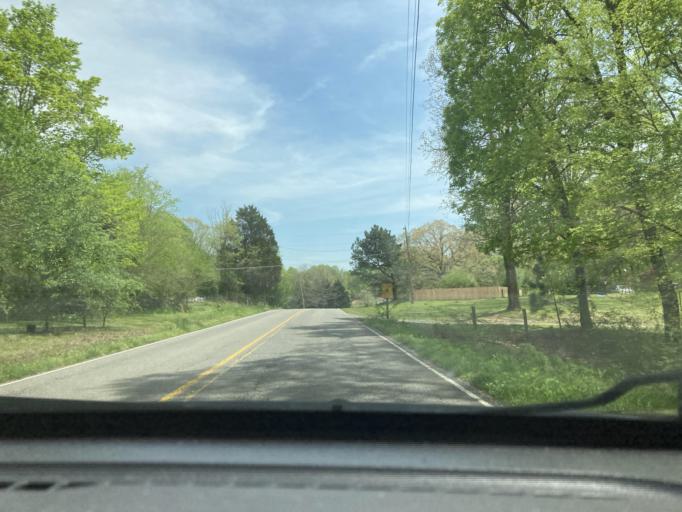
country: US
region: Tennessee
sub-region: Dickson County
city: Charlotte
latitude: 36.2681
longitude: -87.2368
